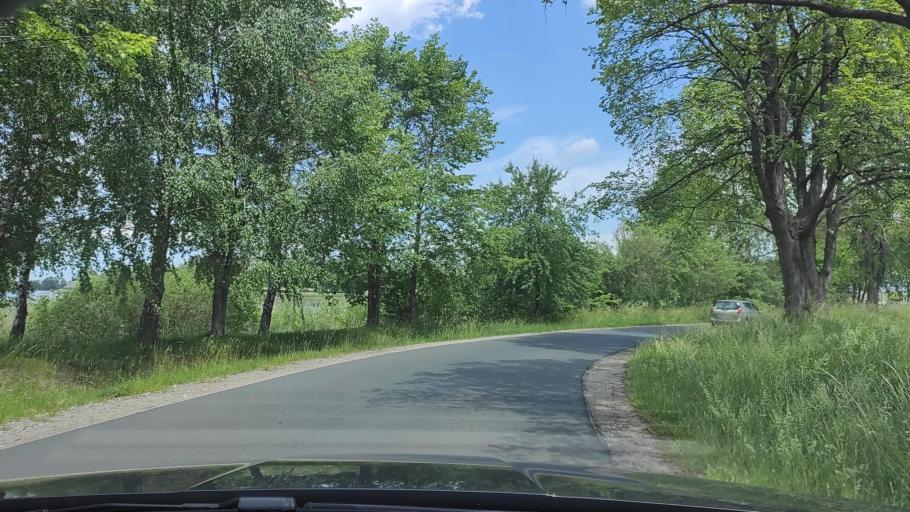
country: PL
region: Greater Poland Voivodeship
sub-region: Powiat gnieznienski
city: Lubowo
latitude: 52.5232
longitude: 17.3834
